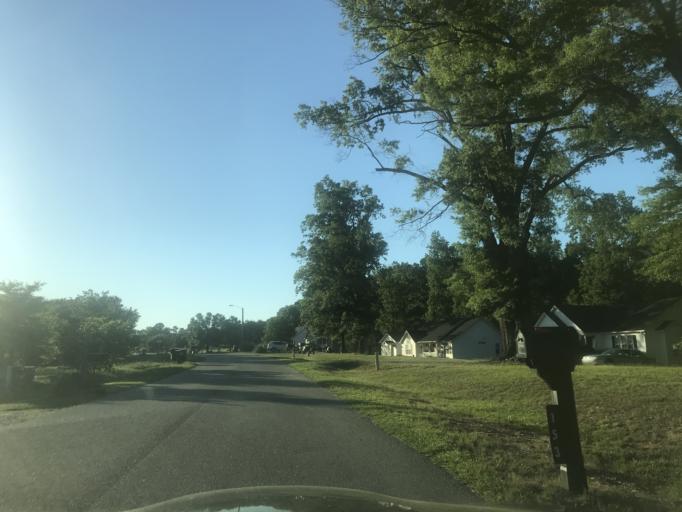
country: US
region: North Carolina
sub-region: Johnston County
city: Archer Lodge
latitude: 35.6824
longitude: -78.3413
